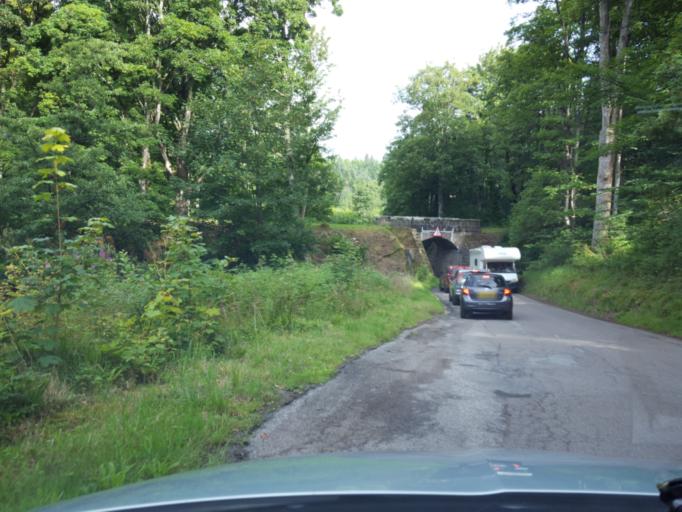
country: GB
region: Scotland
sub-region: Moray
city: Rothes
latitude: 57.4787
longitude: -3.1999
